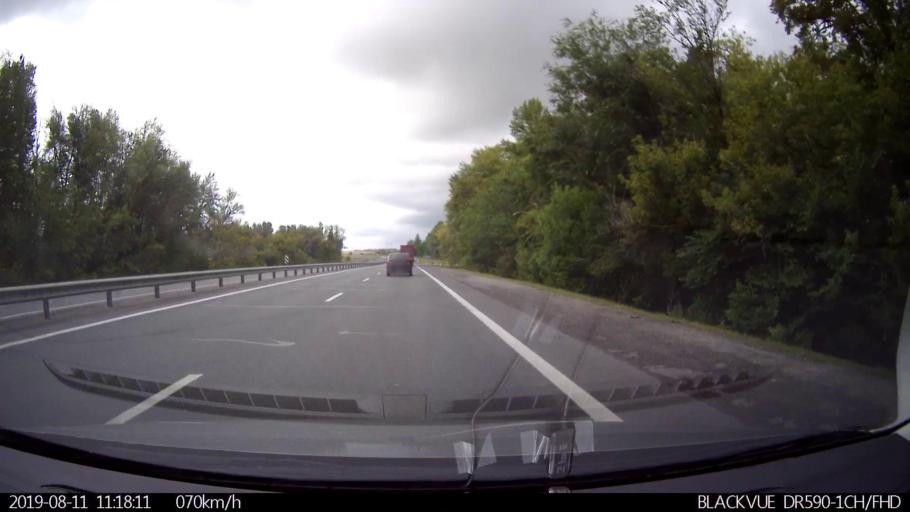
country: RU
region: Ulyanovsk
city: Novoul'yanovsk
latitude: 54.1822
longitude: 48.2705
